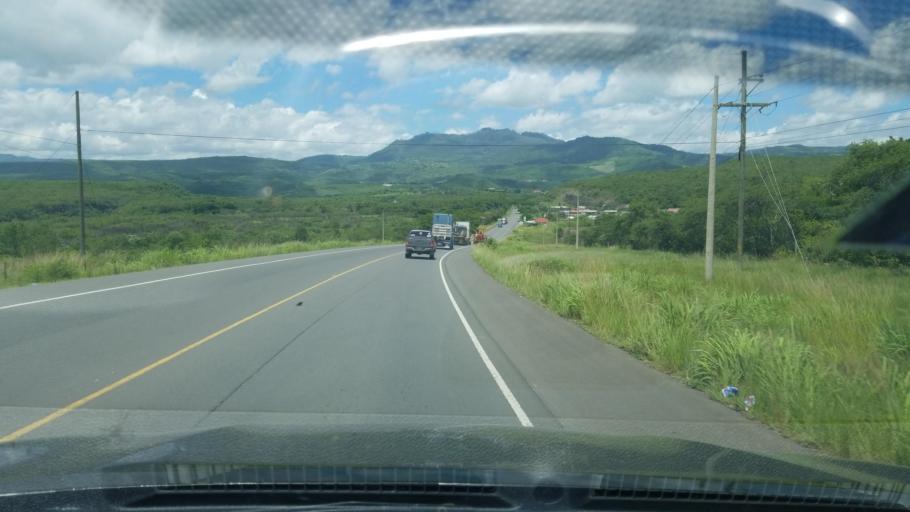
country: HN
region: Francisco Morazan
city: Cofradia
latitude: 14.2802
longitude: -87.2436
